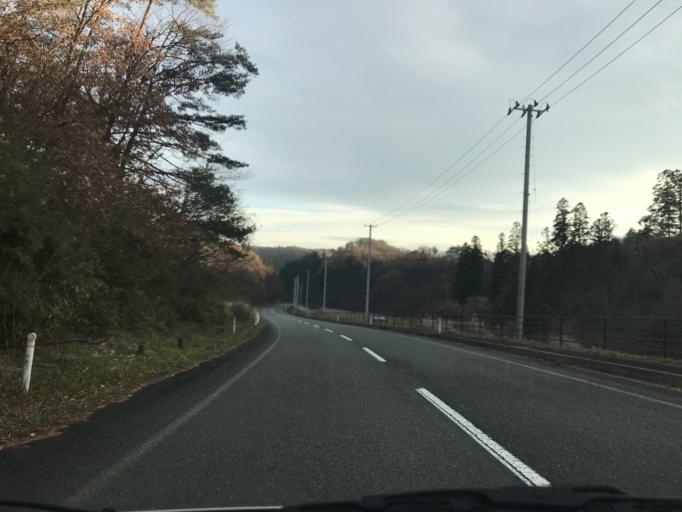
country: JP
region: Iwate
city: Ichinoseki
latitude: 38.9770
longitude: 141.0715
